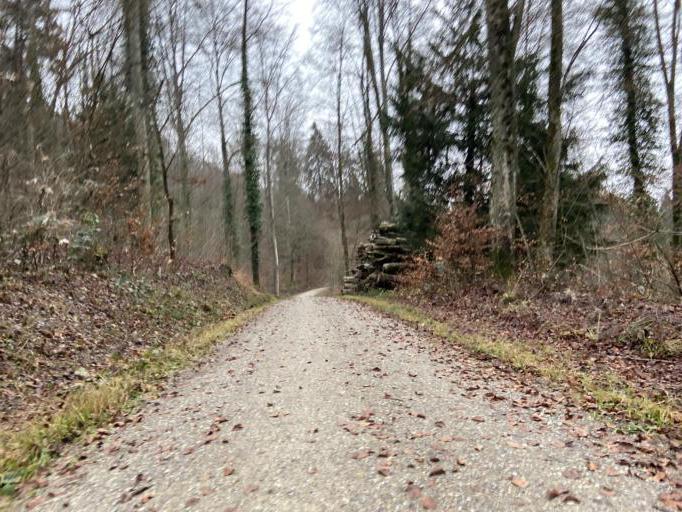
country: CH
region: Zurich
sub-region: Bezirk Winterthur
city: Toess (Kreis 4) / Vorder-Daettnau
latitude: 47.4870
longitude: 8.6851
